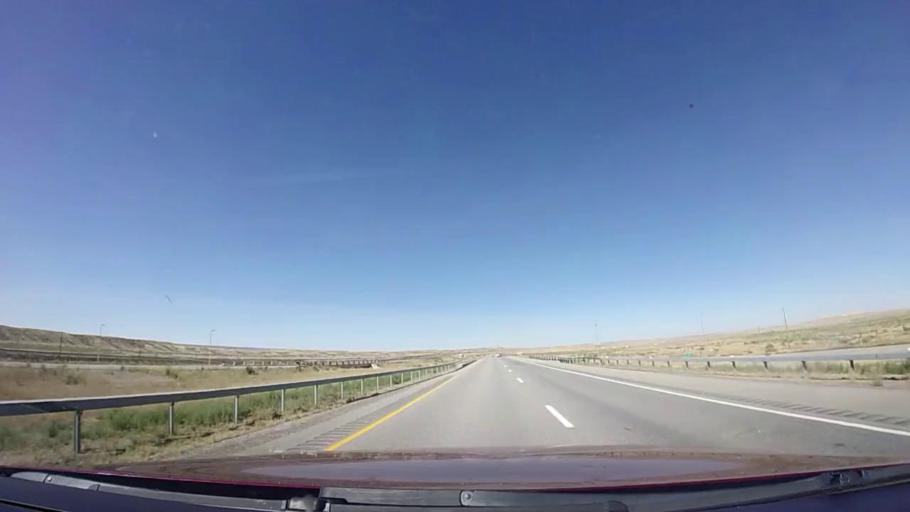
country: US
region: Wyoming
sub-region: Carbon County
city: Rawlins
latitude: 41.6518
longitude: -108.1280
